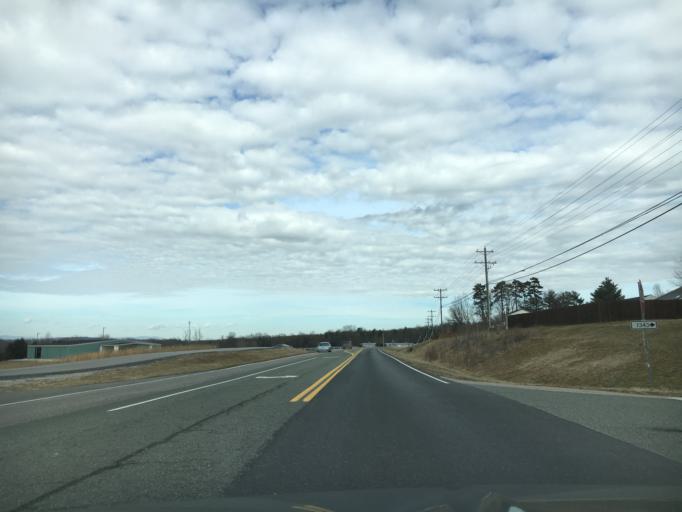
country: US
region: Virginia
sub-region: Augusta County
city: Crimora
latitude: 38.1364
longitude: -78.8452
